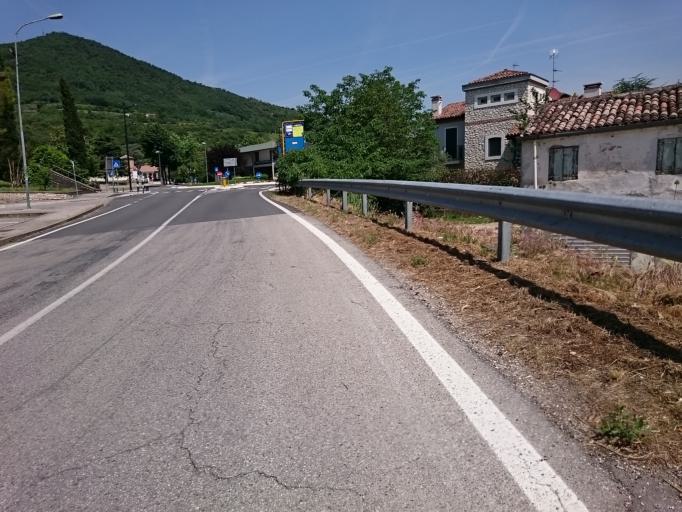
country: IT
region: Veneto
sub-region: Provincia di Padova
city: Lozzo Atestino
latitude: 45.2863
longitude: 11.6272
